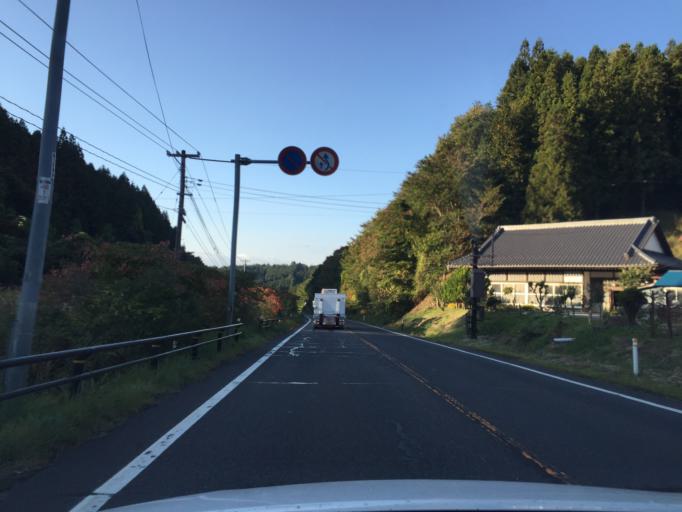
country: JP
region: Fukushima
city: Ishikawa
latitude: 37.2060
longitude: 140.6096
